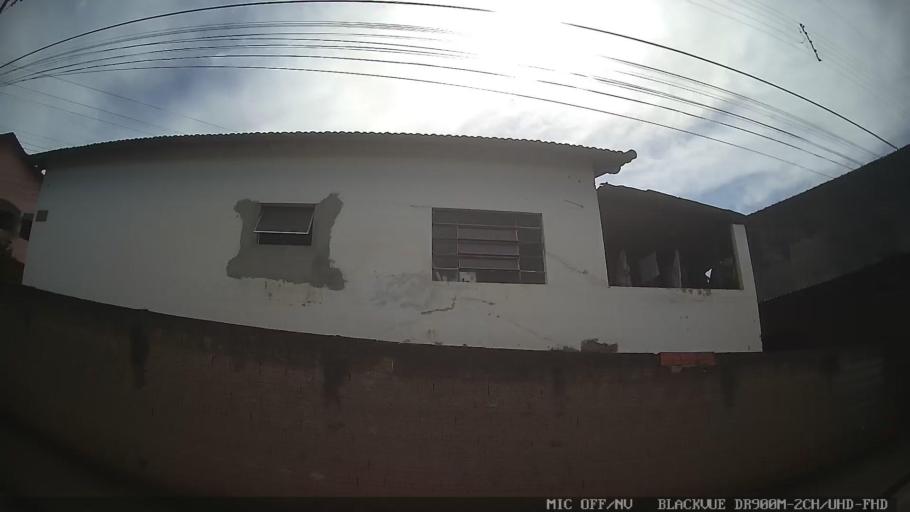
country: BR
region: Sao Paulo
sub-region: Conchas
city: Conchas
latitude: -23.0112
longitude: -48.0039
